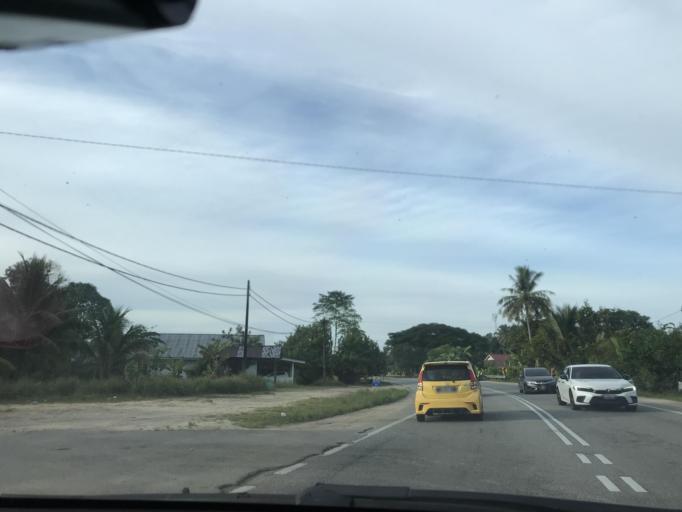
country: MY
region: Kelantan
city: Kampong Kadok
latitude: 5.9844
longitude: 102.1895
